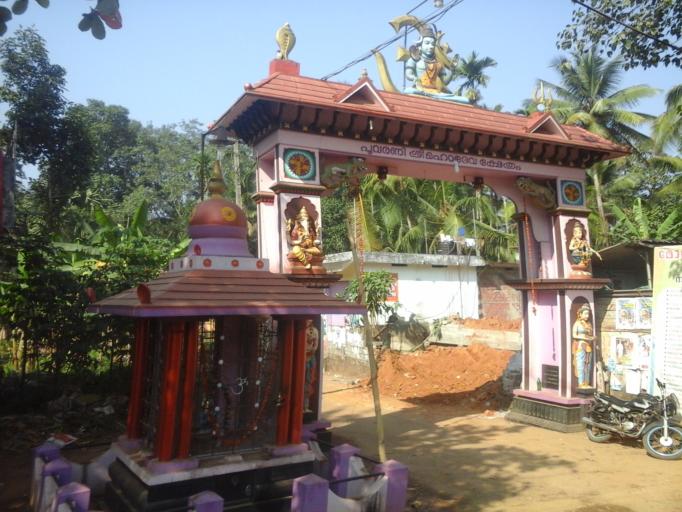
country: IN
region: Kerala
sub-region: Kottayam
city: Lalam
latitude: 9.6778
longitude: 76.6960
